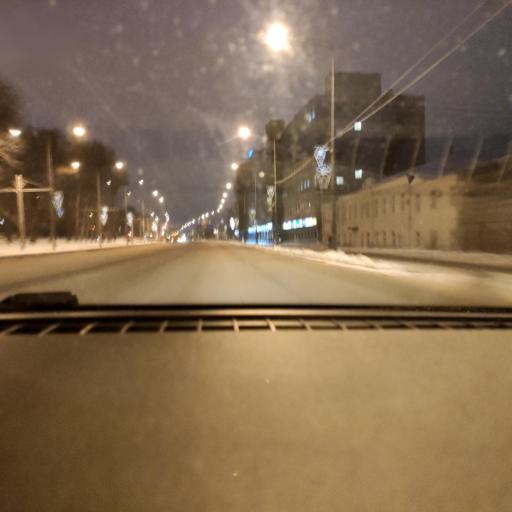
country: RU
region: Samara
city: Samara
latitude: 53.2187
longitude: 50.1514
